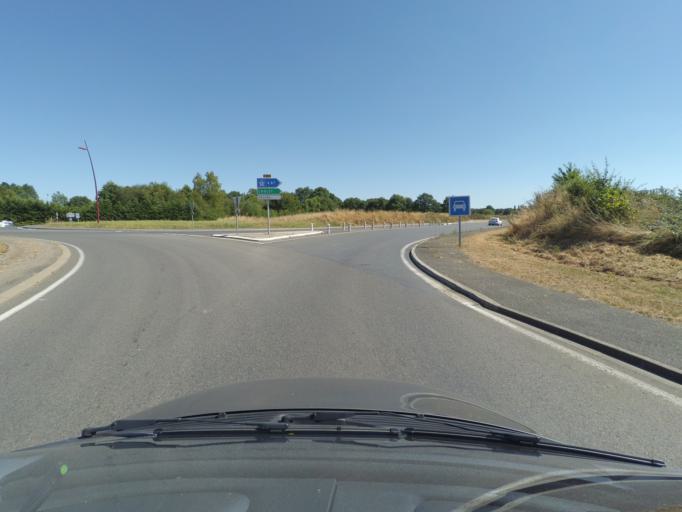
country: FR
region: Pays de la Loire
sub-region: Departement de Maine-et-Loire
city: Coron
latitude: 47.1275
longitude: -0.6375
